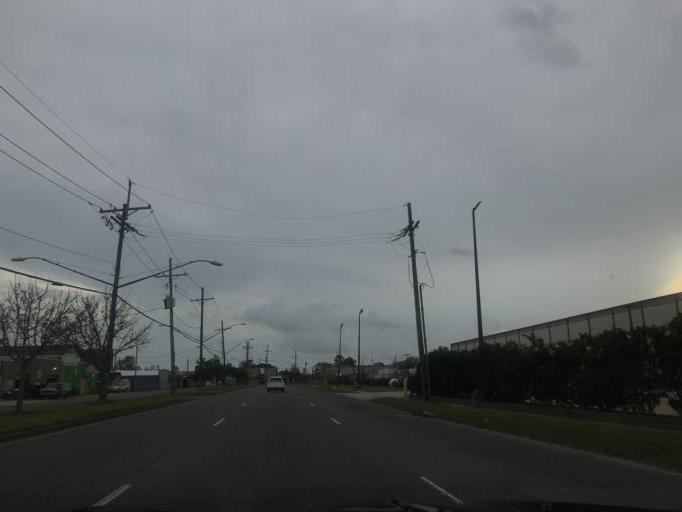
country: US
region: Louisiana
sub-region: Jefferson Parish
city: Jefferson
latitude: 29.9642
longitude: -90.1400
